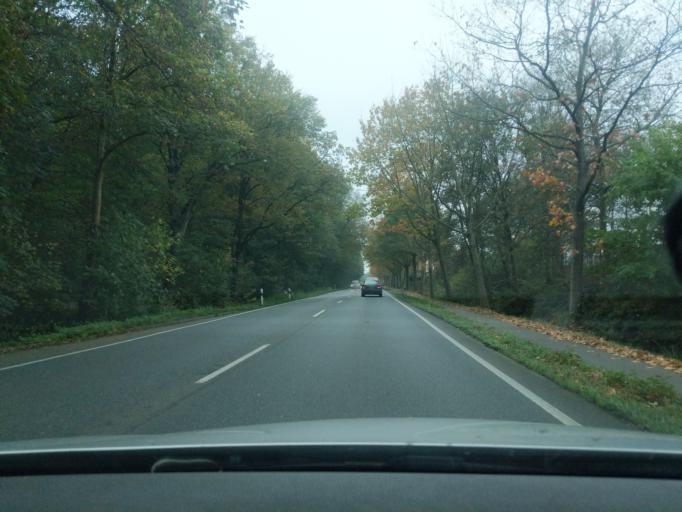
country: DE
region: Lower Saxony
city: Himmelpforten
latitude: 53.6071
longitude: 9.3168
